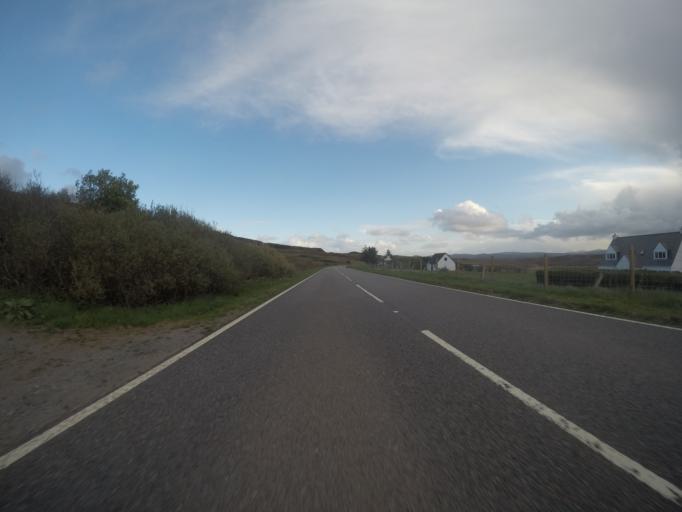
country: GB
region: Scotland
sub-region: Highland
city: Portree
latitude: 57.5615
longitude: -6.3640
